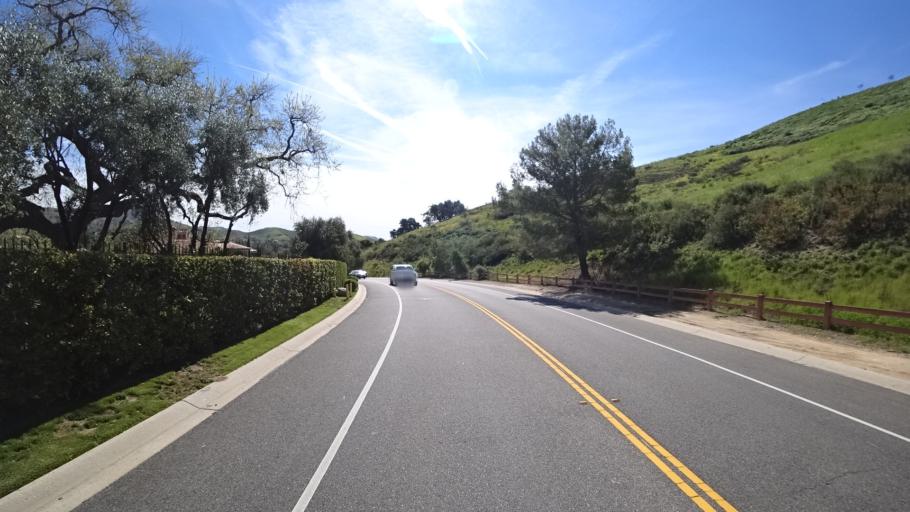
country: US
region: California
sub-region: Ventura County
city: Oak Park
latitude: 34.1860
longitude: -118.7950
